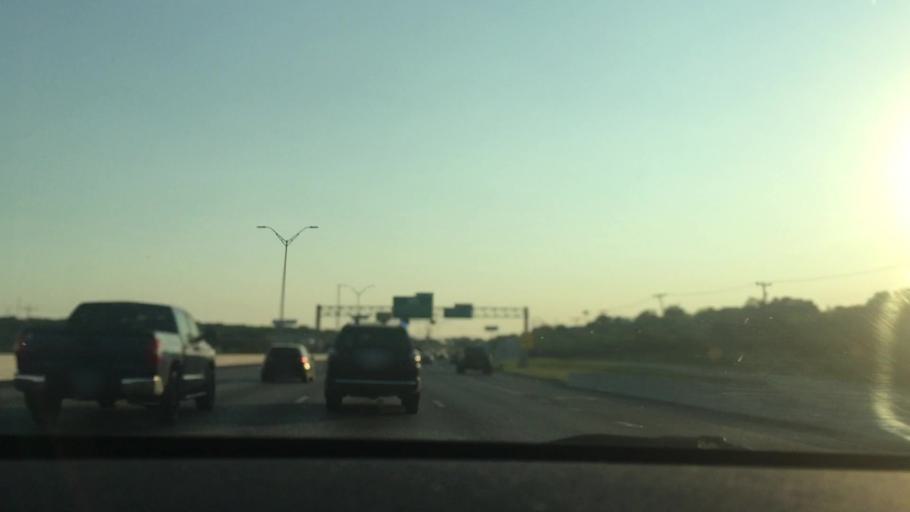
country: US
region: Texas
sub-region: Bexar County
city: Live Oak
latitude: 29.5554
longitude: -98.3483
